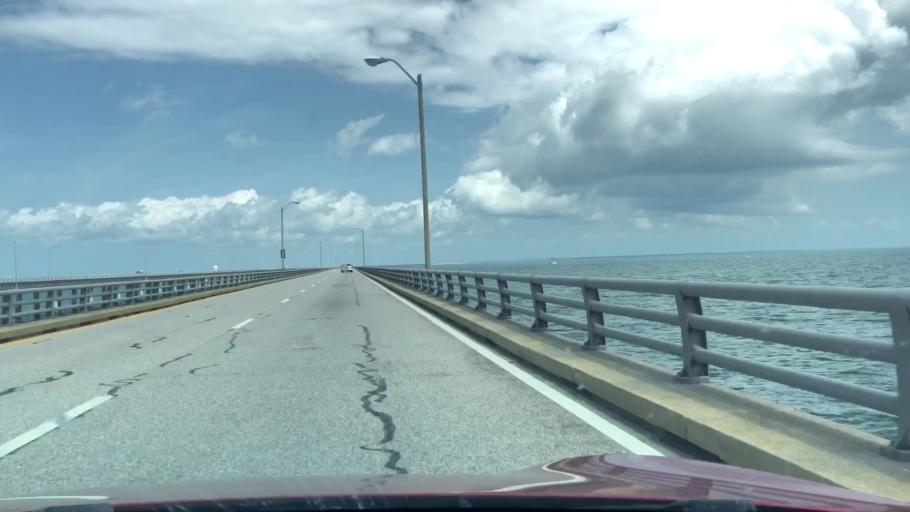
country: US
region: Virginia
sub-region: City of Virginia Beach
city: Virginia Beach
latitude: 37.0002
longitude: -76.0986
